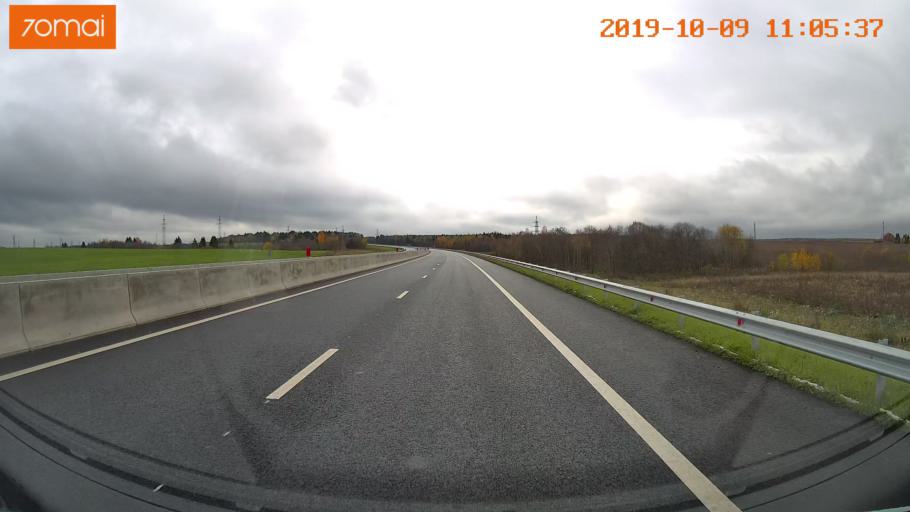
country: RU
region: Vologda
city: Molochnoye
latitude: 59.1975
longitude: 39.7581
